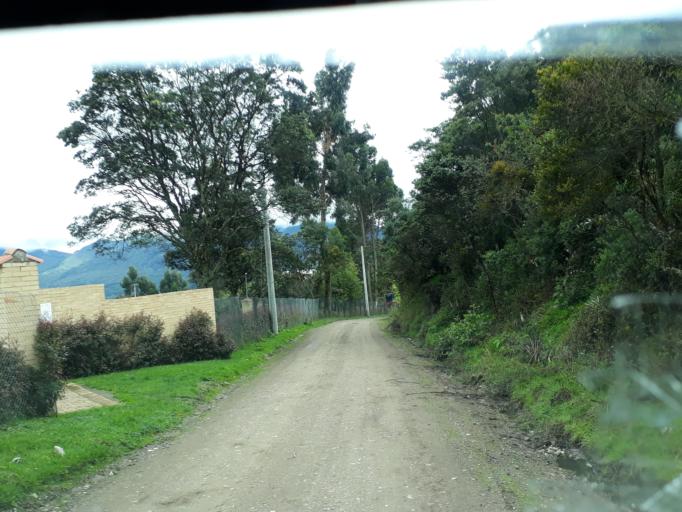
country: CO
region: Cundinamarca
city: Cogua
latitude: 5.1548
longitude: -73.9830
